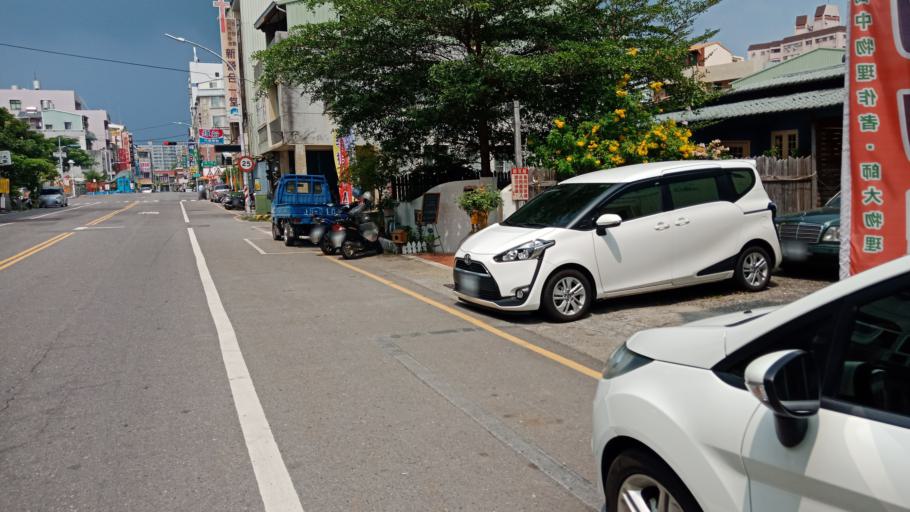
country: TW
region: Taiwan
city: Xinying
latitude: 23.3090
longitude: 120.3226
